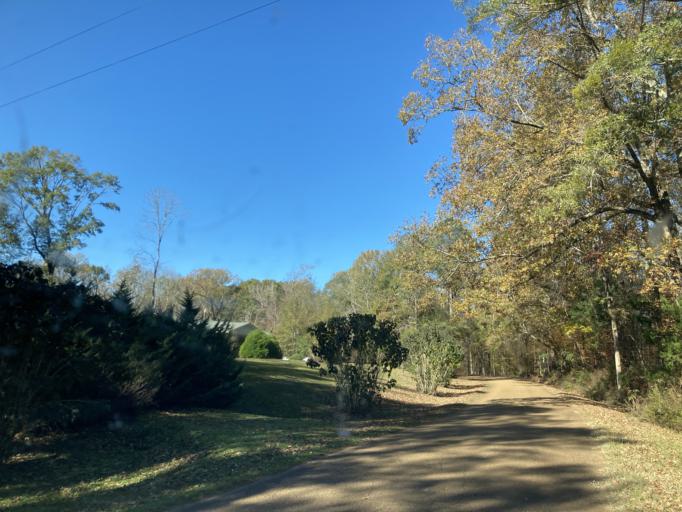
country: US
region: Mississippi
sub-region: Hinds County
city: Lynchburg
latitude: 32.5887
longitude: -90.5208
